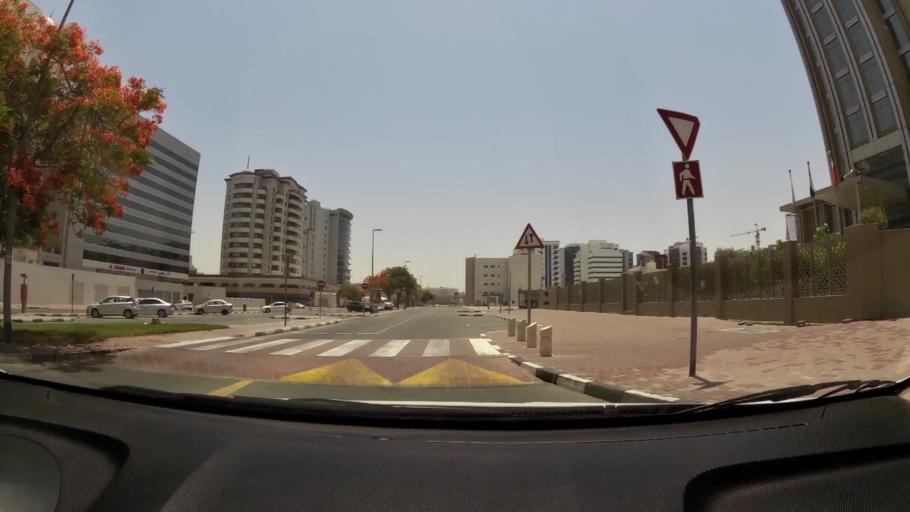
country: AE
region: Ash Shariqah
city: Sharjah
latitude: 25.2562
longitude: 55.3325
